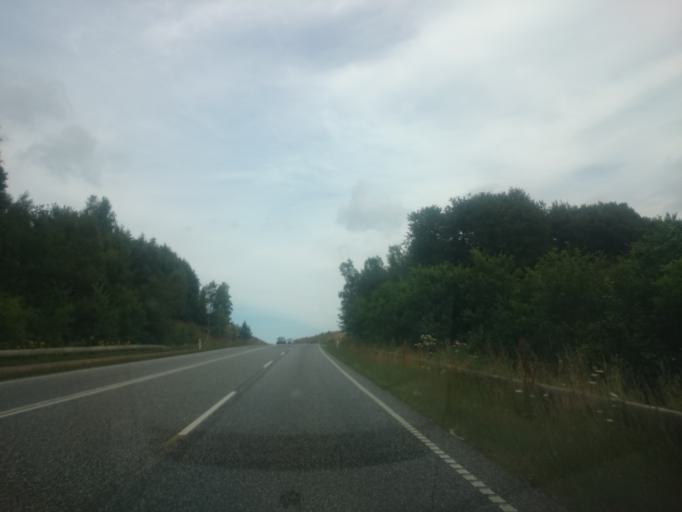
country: DK
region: South Denmark
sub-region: Vejle Kommune
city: Jelling
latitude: 55.6881
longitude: 9.3800
